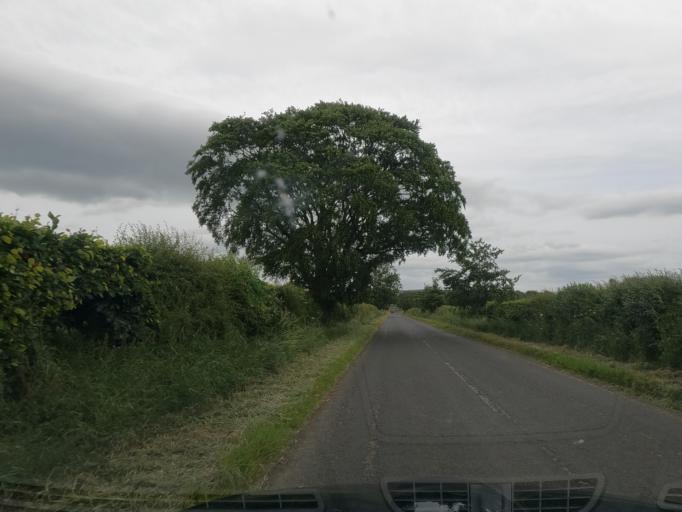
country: GB
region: England
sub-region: Northumberland
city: Doddington
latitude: 55.5615
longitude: -1.9317
